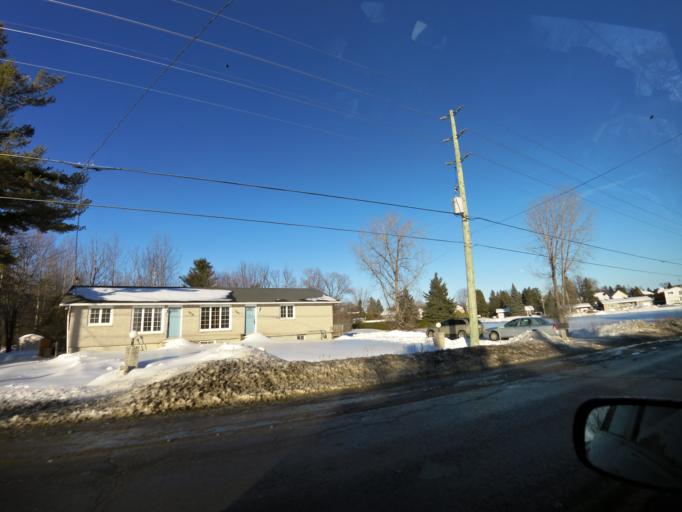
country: CA
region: Ontario
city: Ottawa
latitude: 45.4310
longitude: -75.5203
